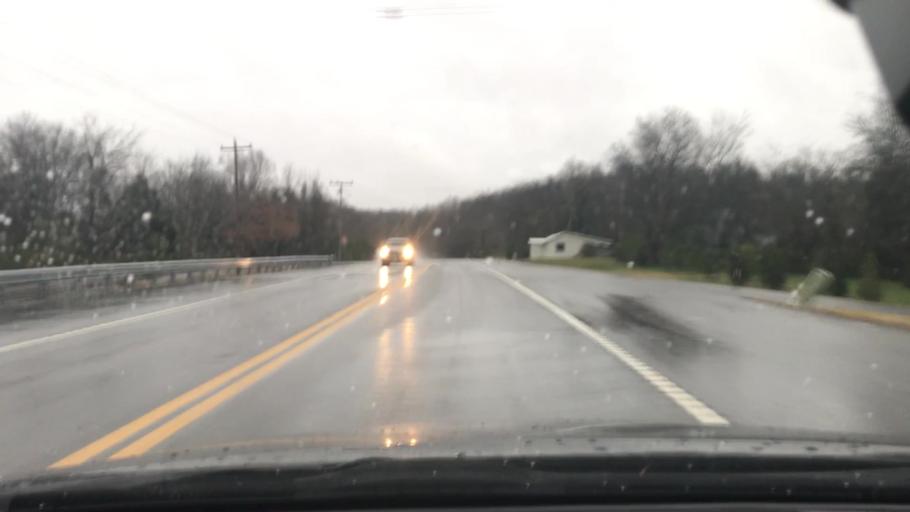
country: US
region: Tennessee
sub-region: Cheatham County
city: Ashland City
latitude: 36.2818
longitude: -87.1448
